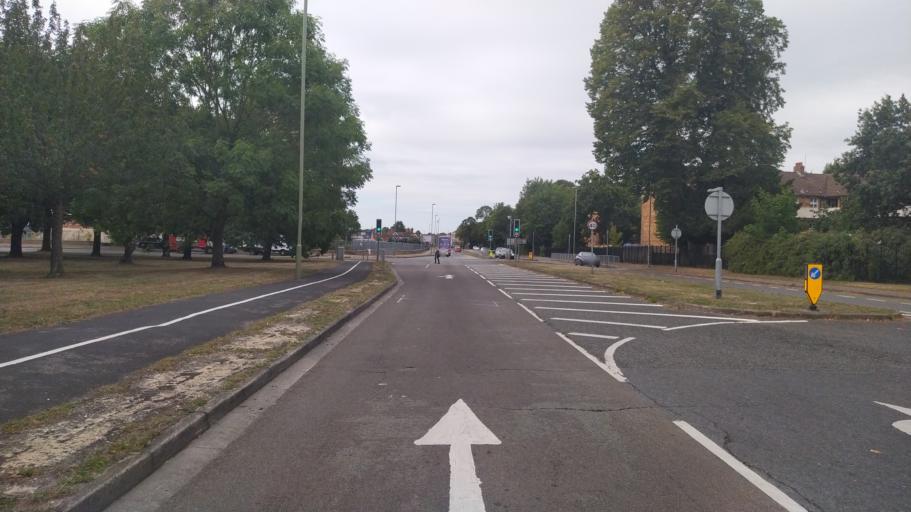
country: GB
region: England
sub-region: Hampshire
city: Havant
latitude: 50.8688
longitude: -0.9758
